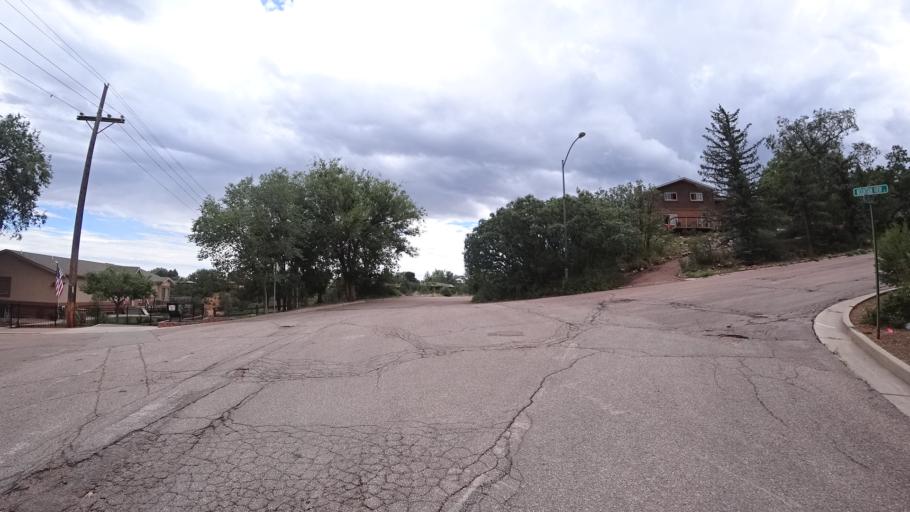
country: US
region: Colorado
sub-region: El Paso County
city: Manitou Springs
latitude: 38.8534
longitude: -104.8928
